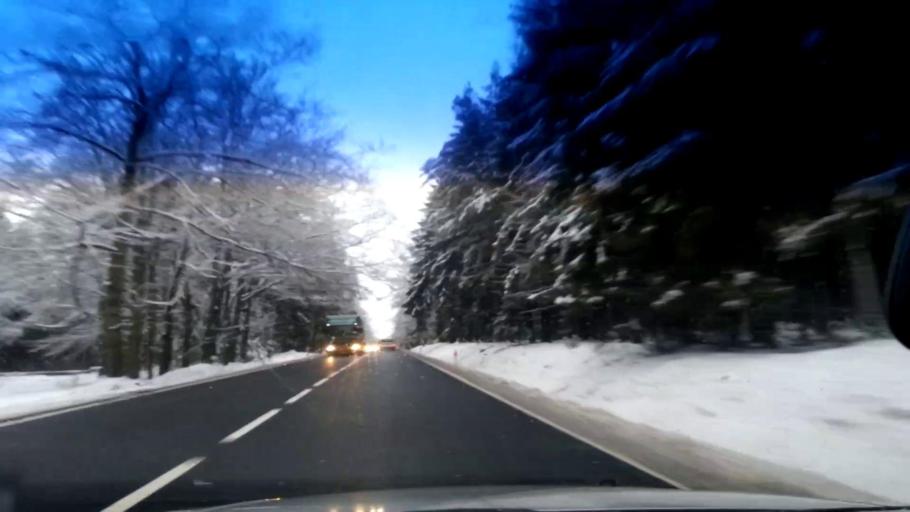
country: CZ
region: Karlovarsky
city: Hazlov
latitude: 50.1769
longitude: 12.2524
